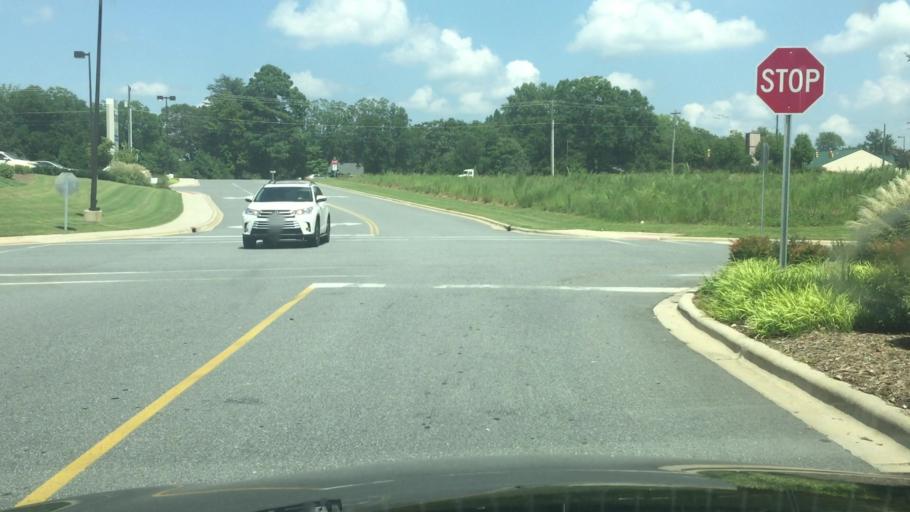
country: US
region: North Carolina
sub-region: Rowan County
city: Salisbury
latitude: 35.6313
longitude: -80.4890
